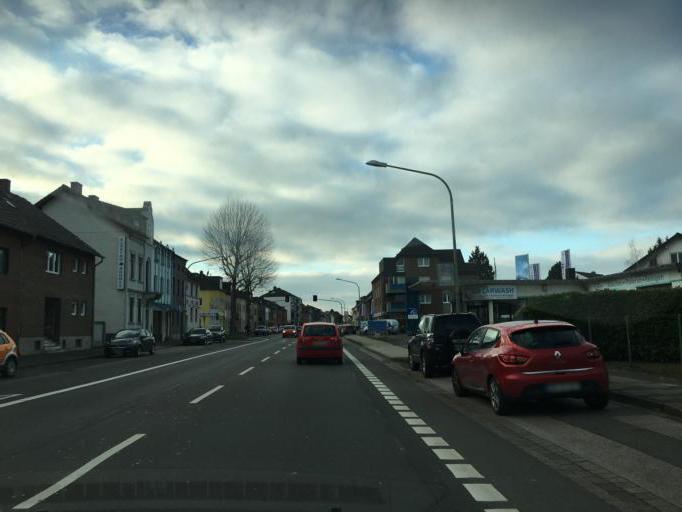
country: DE
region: North Rhine-Westphalia
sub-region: Regierungsbezirk Koln
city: Dueren
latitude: 50.7970
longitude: 6.4581
